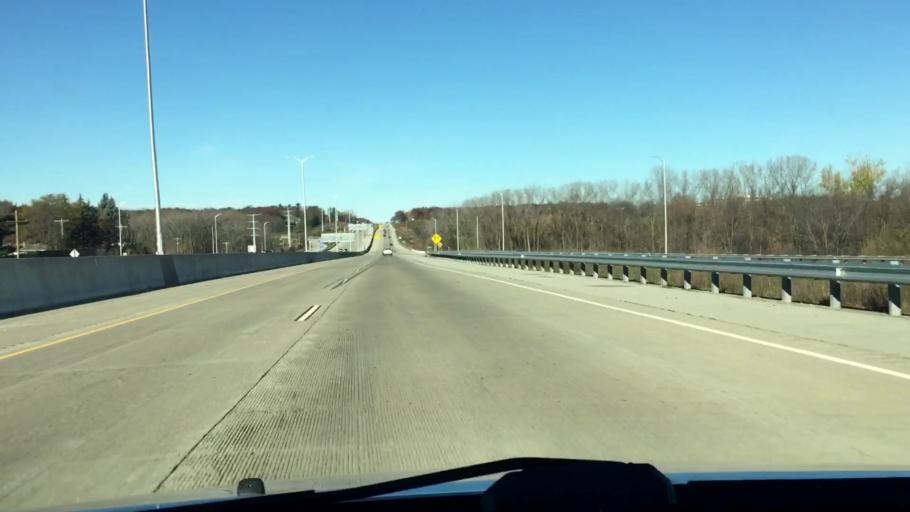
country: US
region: Wisconsin
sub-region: Brown County
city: Howard
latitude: 44.5442
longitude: -88.0905
